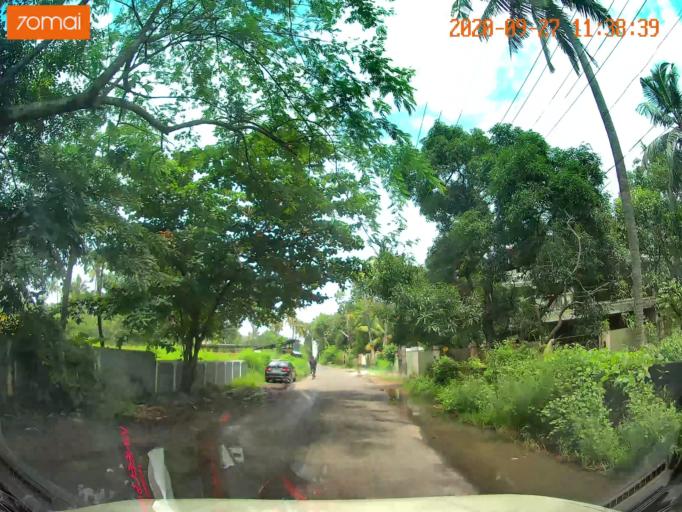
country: IN
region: Kerala
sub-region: Thrissur District
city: Thanniyam
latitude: 10.4609
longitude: 76.1204
